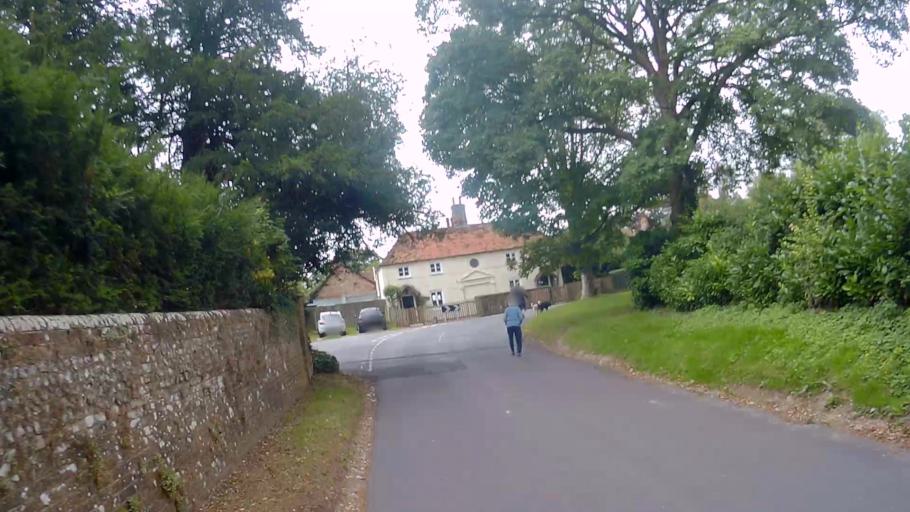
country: GB
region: England
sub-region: Hampshire
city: Basingstoke
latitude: 51.2109
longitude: -1.1595
